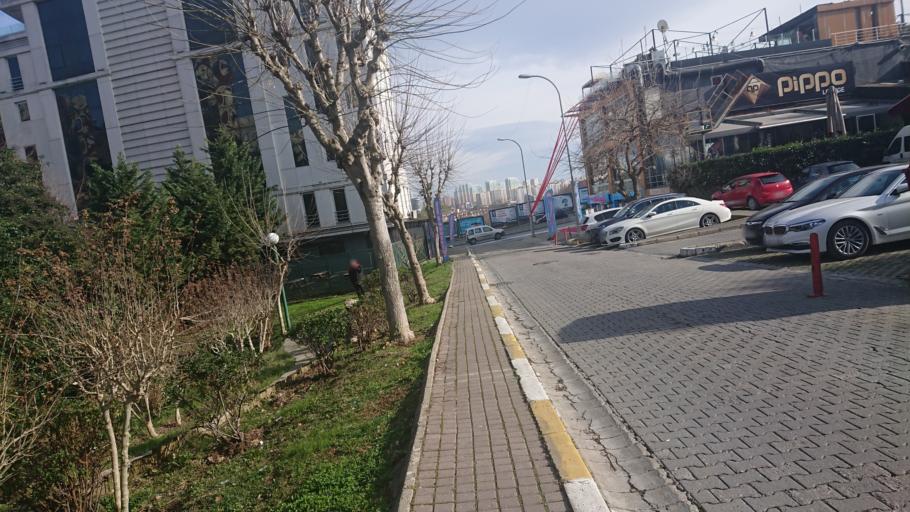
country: TR
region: Istanbul
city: Esenyurt
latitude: 41.0696
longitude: 28.6833
